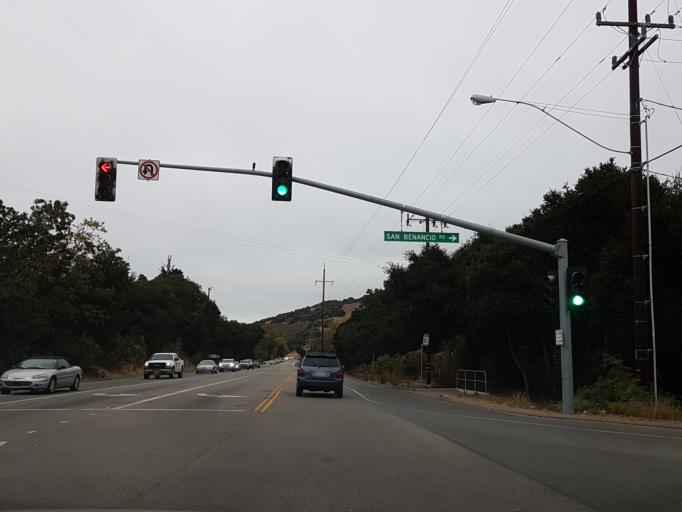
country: US
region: California
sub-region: Monterey County
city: Carmel Valley Village
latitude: 36.5798
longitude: -121.7207
